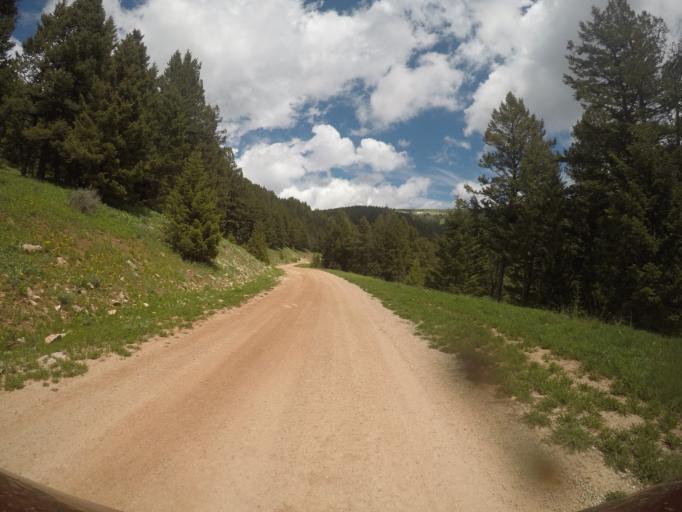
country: US
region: Wyoming
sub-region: Big Horn County
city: Lovell
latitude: 45.1688
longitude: -108.4156
